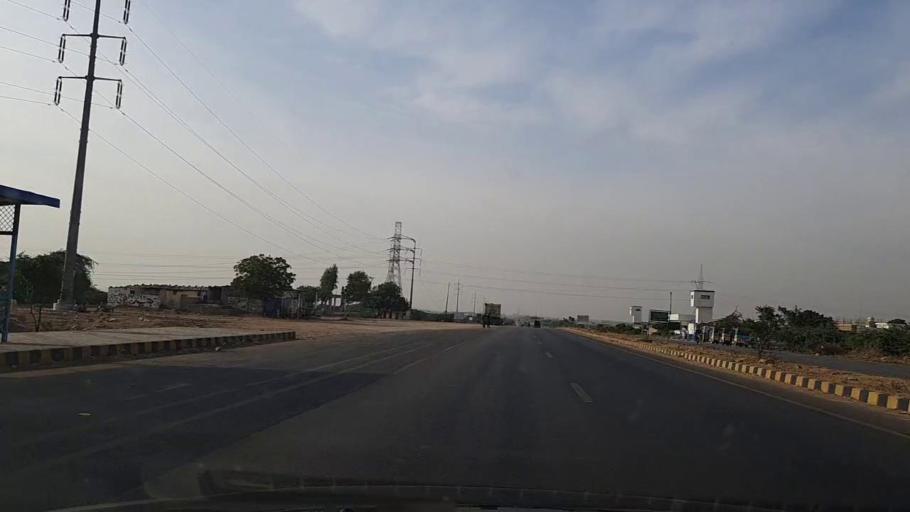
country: PK
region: Sindh
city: Gharo
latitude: 24.7662
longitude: 67.5518
